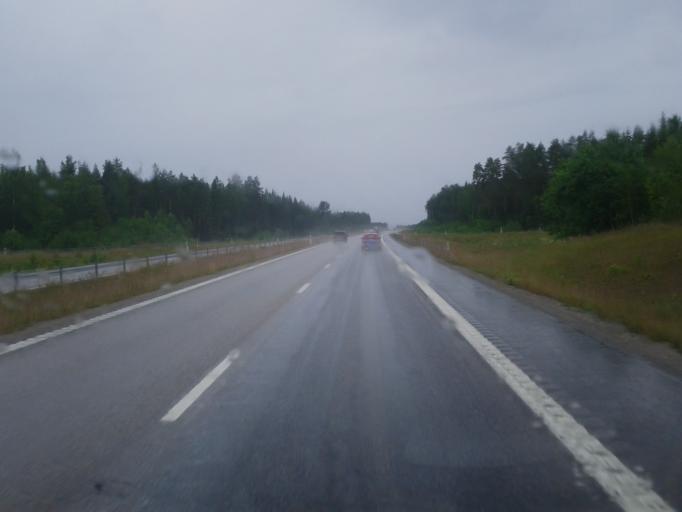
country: SE
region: Uppsala
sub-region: Tierps Kommun
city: Tierp
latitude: 60.2165
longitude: 17.4962
